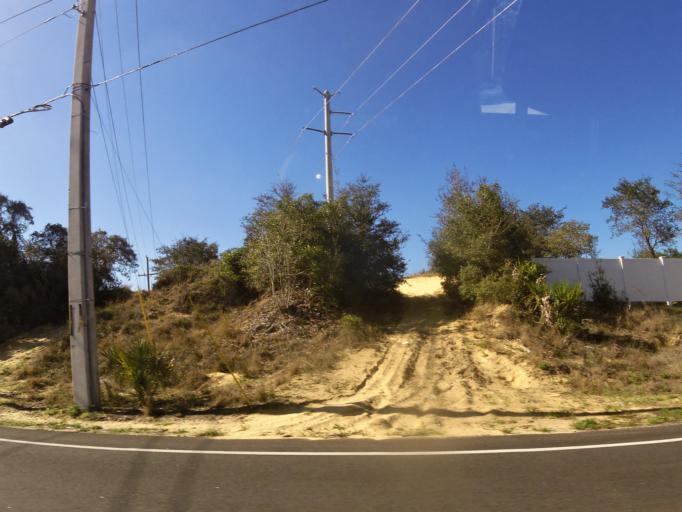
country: US
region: Florida
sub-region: Brevard County
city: Port Saint John
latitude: 28.5321
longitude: -80.8087
